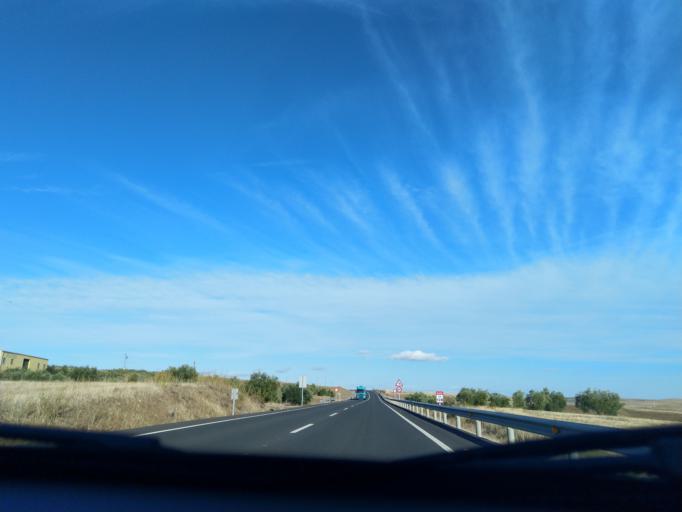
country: ES
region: Extremadura
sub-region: Provincia de Badajoz
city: Ahillones
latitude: 38.2641
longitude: -5.8558
